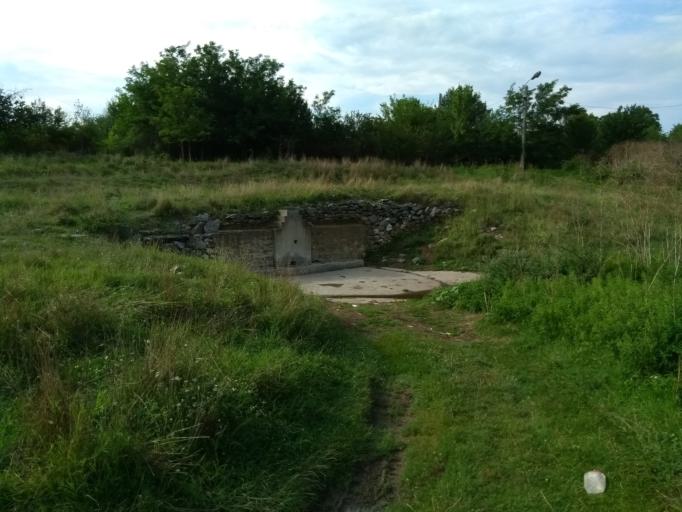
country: BG
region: Sliven
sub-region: Obshtina Sliven
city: Kermen
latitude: 42.4529
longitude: 26.1454
